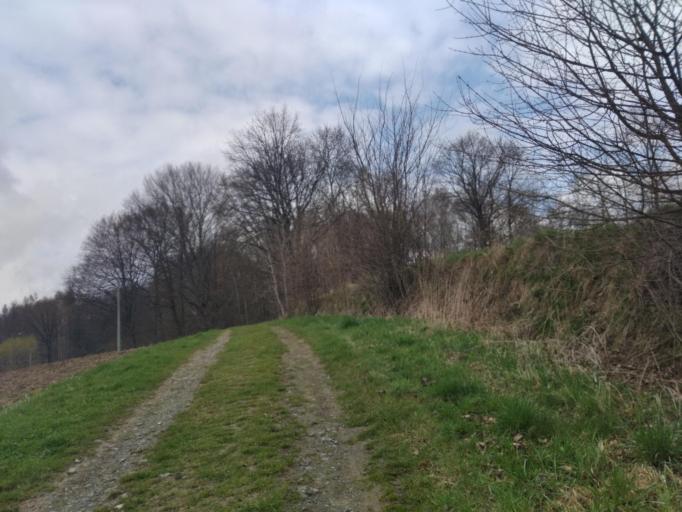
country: PL
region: Subcarpathian Voivodeship
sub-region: Powiat strzyzowski
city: Wisniowa
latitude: 49.8787
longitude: 21.6901
